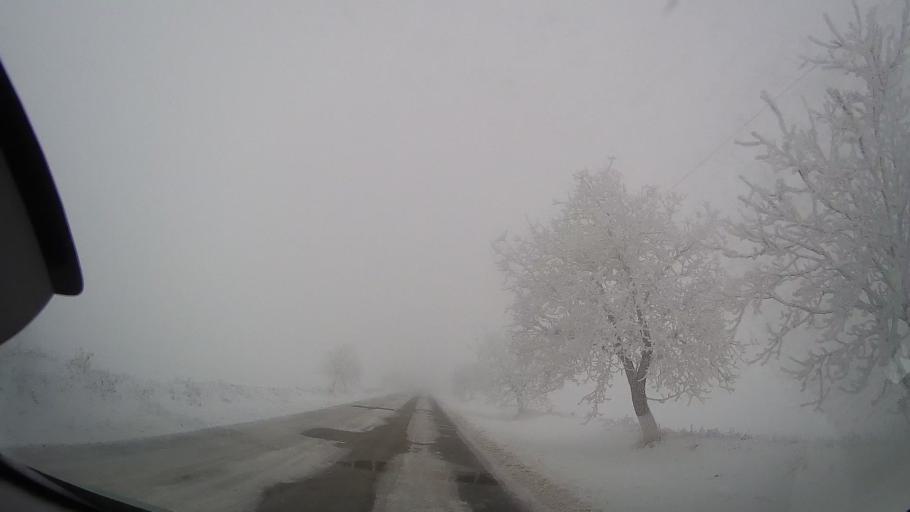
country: RO
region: Neamt
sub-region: Comuna Valea Ursului
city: Valea Ursului
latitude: 46.8050
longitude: 27.0714
